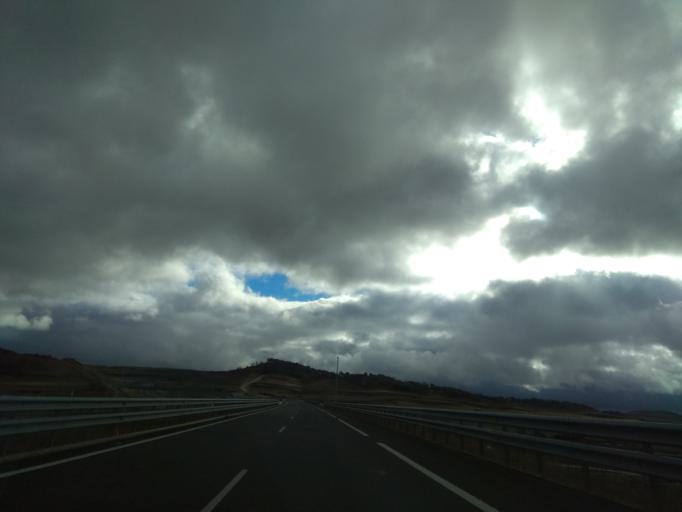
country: ES
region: Castille and Leon
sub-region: Provincia de Burgos
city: Sotragero
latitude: 42.3884
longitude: -3.6929
